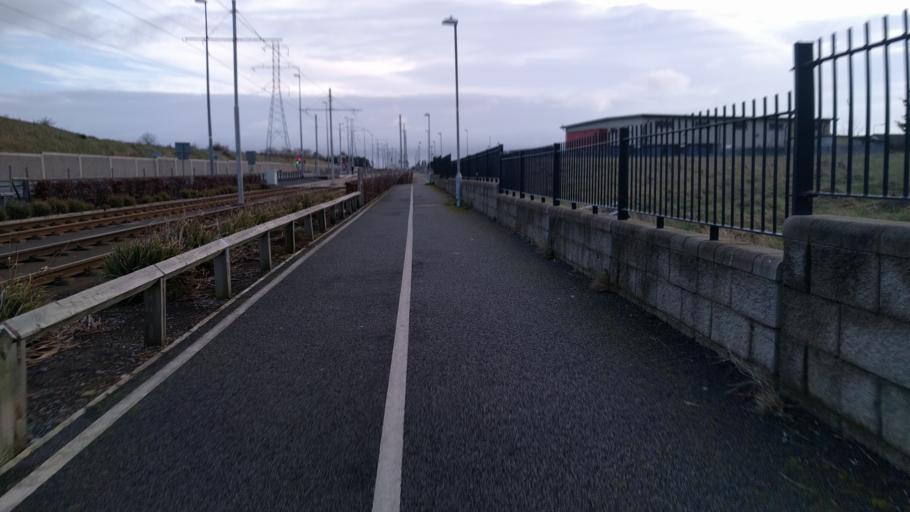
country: IE
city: Jobstown
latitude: 53.2925
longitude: -6.3982
